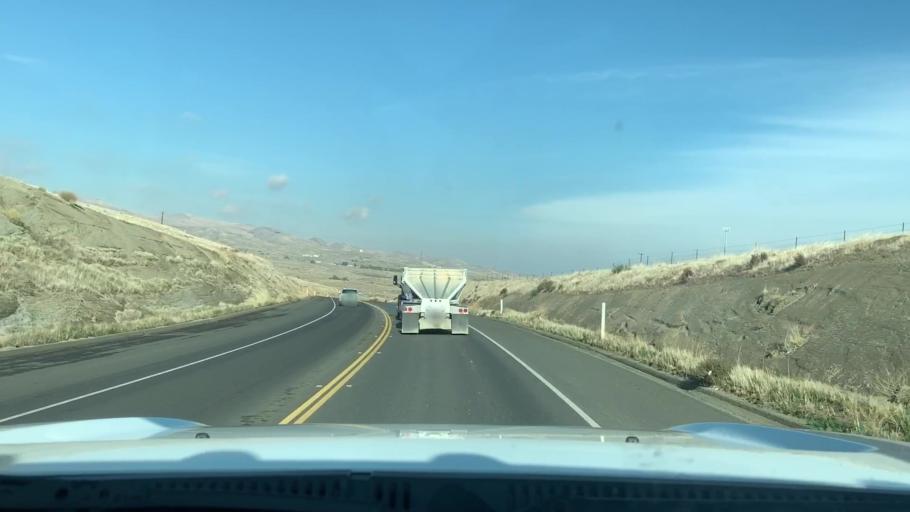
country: US
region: California
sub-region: Fresno County
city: Coalinga
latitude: 36.2189
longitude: -120.3111
